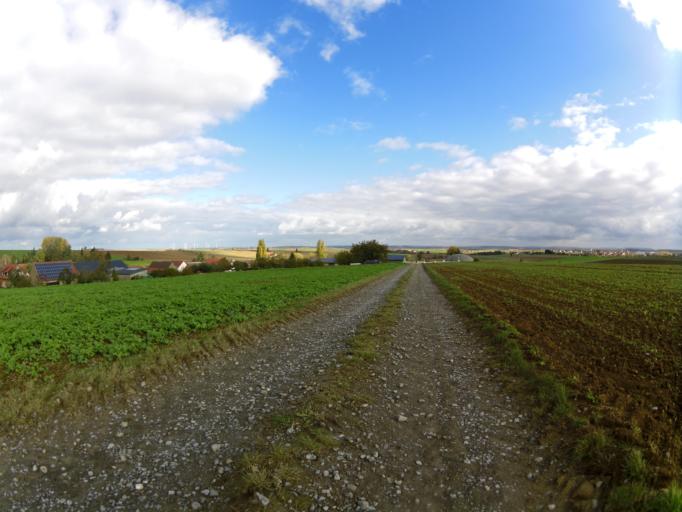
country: DE
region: Bavaria
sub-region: Regierungsbezirk Unterfranken
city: Unterpleichfeld
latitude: 49.8824
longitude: 10.0095
